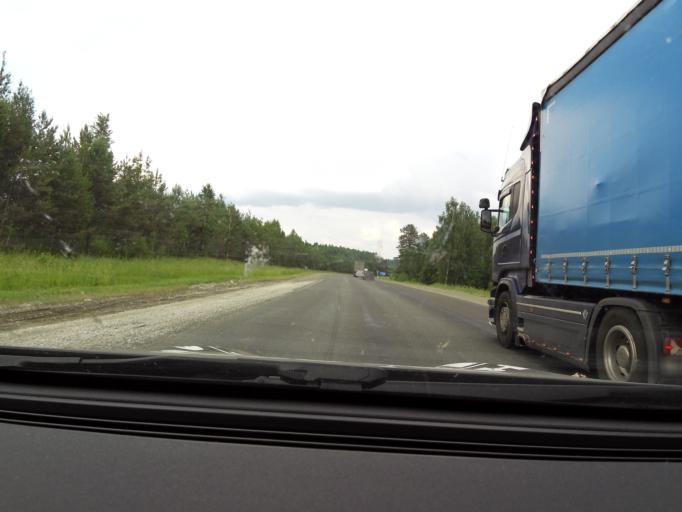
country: RU
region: Sverdlovsk
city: Ufimskiy
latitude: 56.7792
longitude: 58.2588
